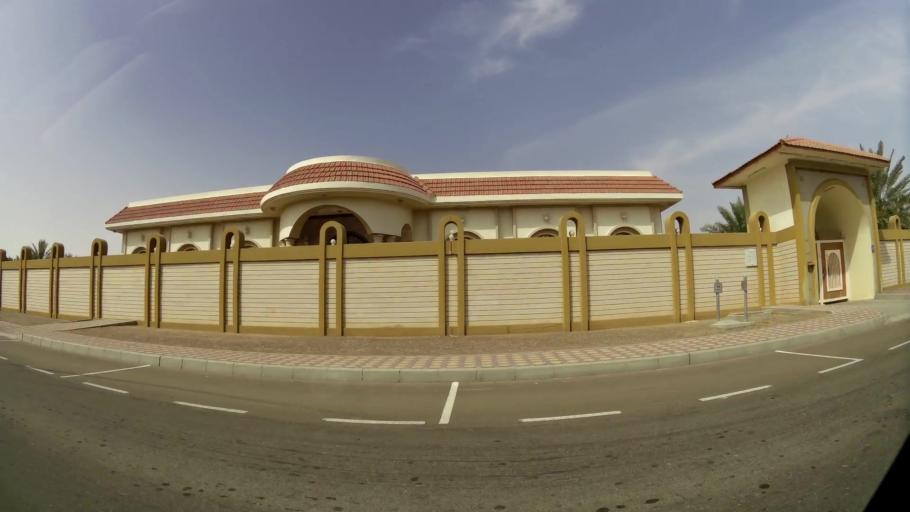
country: AE
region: Abu Dhabi
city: Al Ain
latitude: 24.1695
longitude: 55.7039
